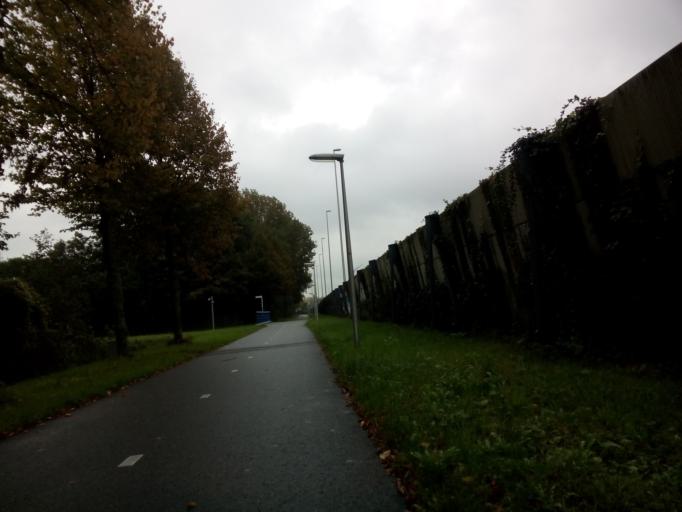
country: NL
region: South Holland
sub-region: Gemeente Zoetermeer
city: Zoetermeer
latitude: 52.0462
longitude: 4.5010
